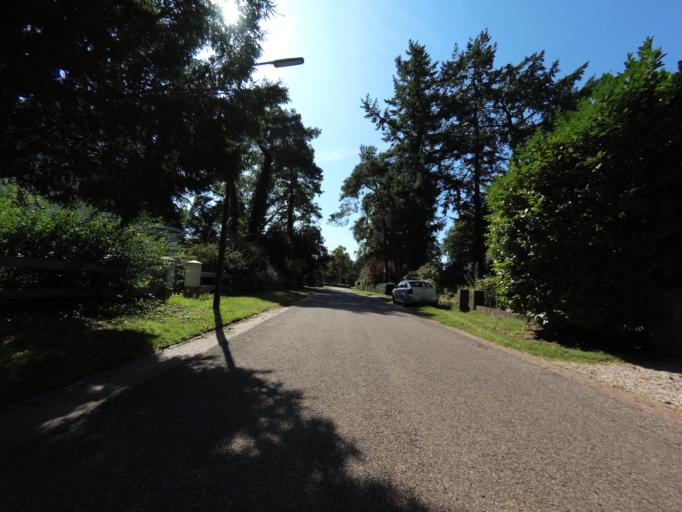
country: NL
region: Utrecht
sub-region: Gemeente Utrechtse Heuvelrug
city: Doorn
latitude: 52.0371
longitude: 5.3483
